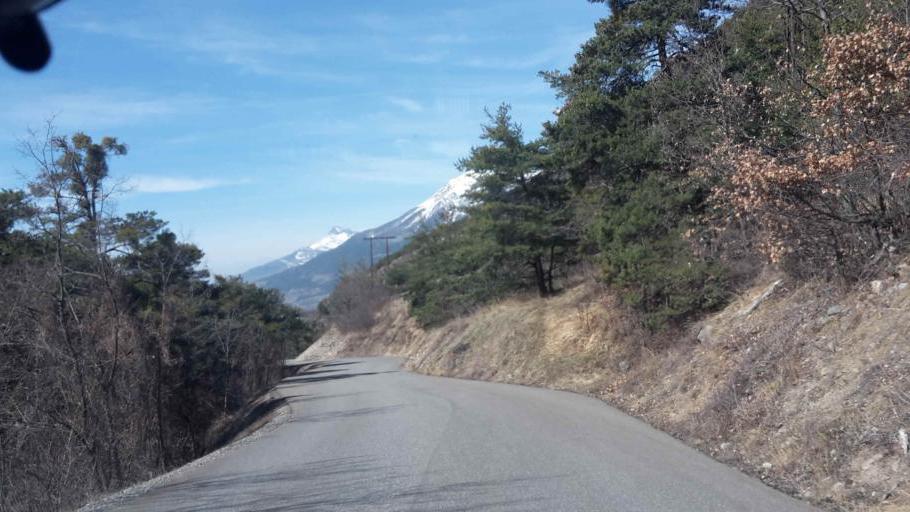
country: FR
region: Provence-Alpes-Cote d'Azur
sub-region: Departement des Hautes-Alpes
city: Embrun
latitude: 44.5572
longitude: 6.5675
